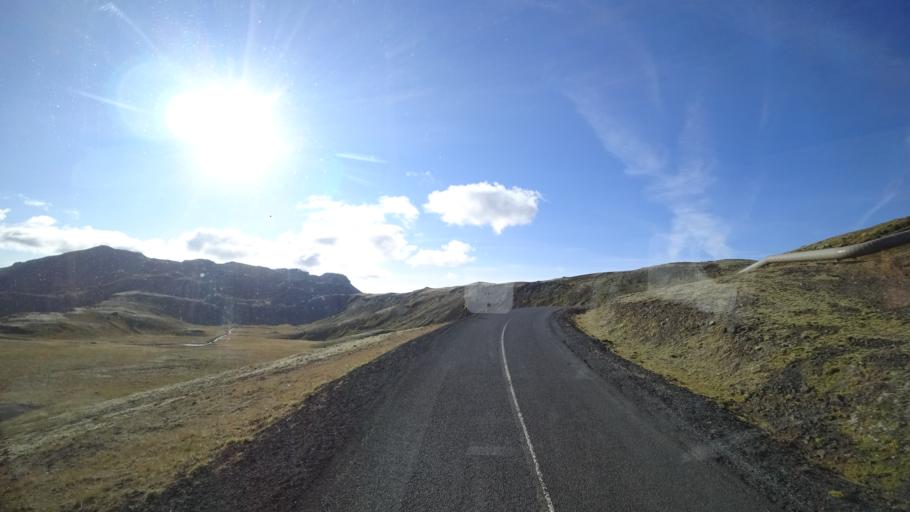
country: IS
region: South
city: Hveragerdi
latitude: 64.1075
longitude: -21.2769
